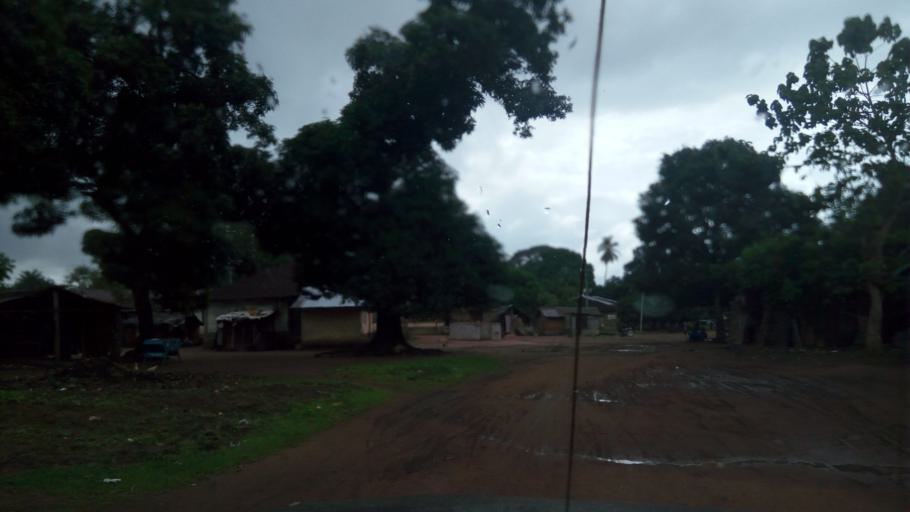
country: SL
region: Northern Province
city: Tintafor
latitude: 8.6395
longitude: -13.2265
